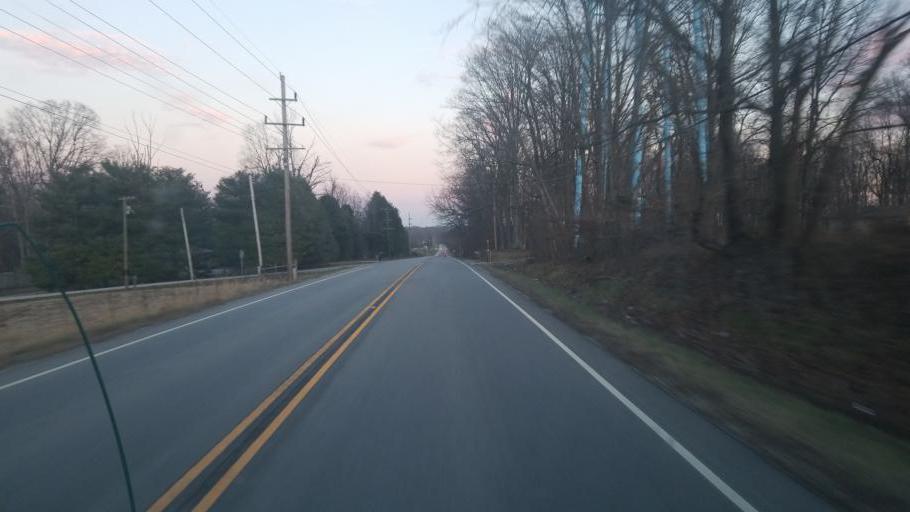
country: US
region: Indiana
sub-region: Lawrence County
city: Bedford
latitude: 38.8745
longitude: -86.3326
